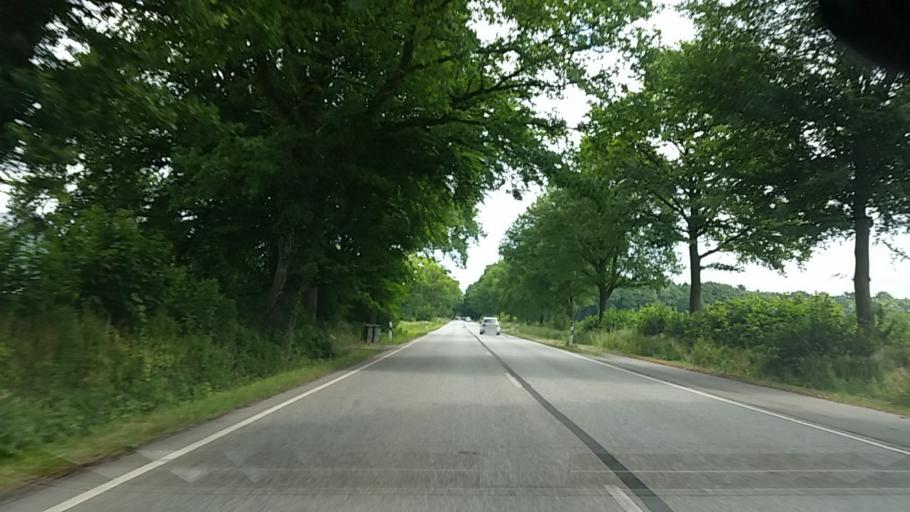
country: DE
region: Schleswig-Holstein
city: Tangstedt
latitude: 53.7313
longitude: 10.1054
